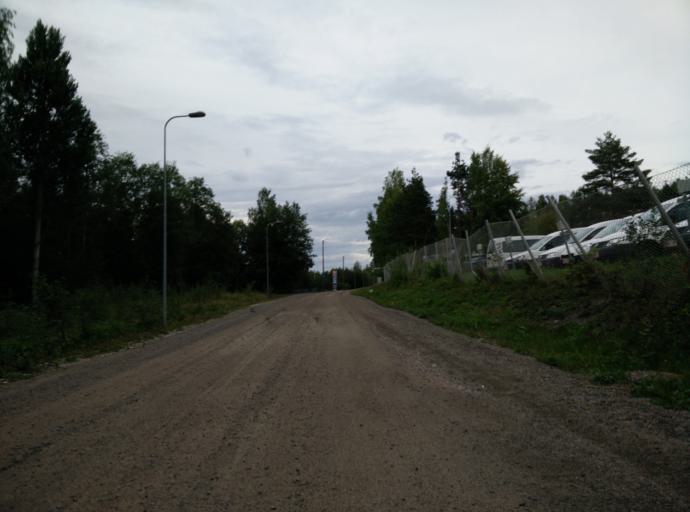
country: FI
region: Haeme
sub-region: Haemeenlinna
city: Haemeenlinna
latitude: 60.9874
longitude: 24.4812
